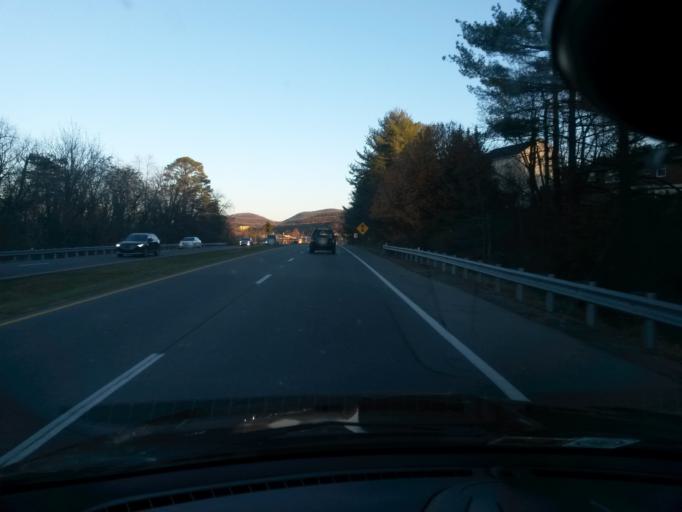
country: US
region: Virginia
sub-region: Roanoke County
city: Cave Spring
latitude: 37.2247
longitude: -79.9945
